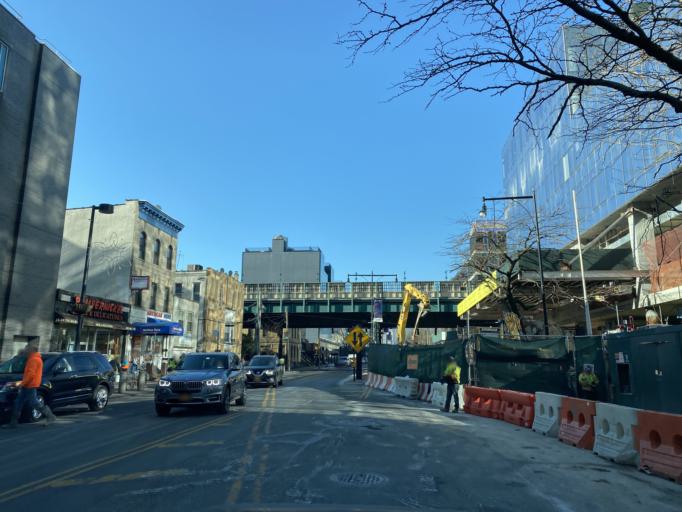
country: US
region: New York
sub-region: Queens County
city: Long Island City
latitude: 40.7475
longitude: -73.9443
